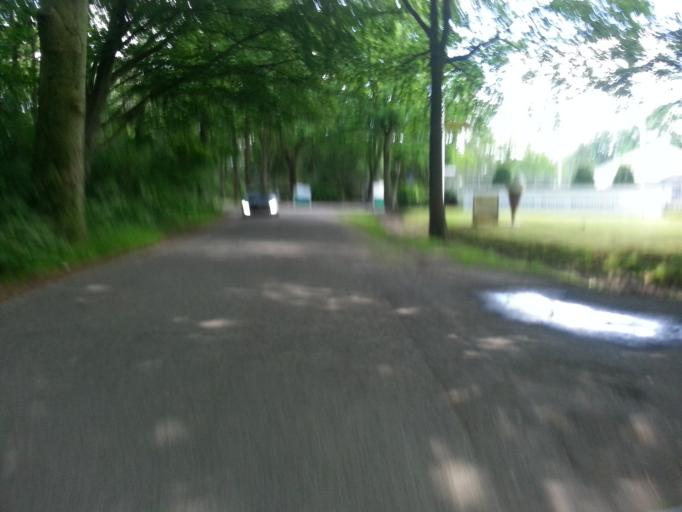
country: NL
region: Utrecht
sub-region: Gemeente Utrechtse Heuvelrug
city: Overberg
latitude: 52.0847
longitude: 5.5146
